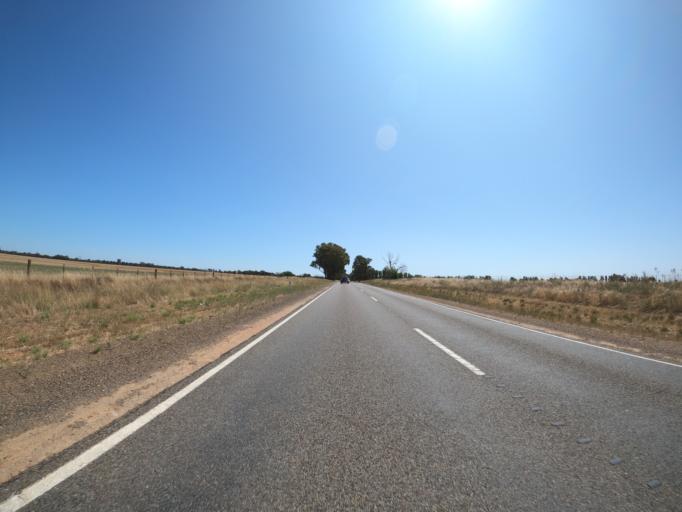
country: AU
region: Victoria
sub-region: Moira
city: Yarrawonga
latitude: -36.0251
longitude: 146.1013
